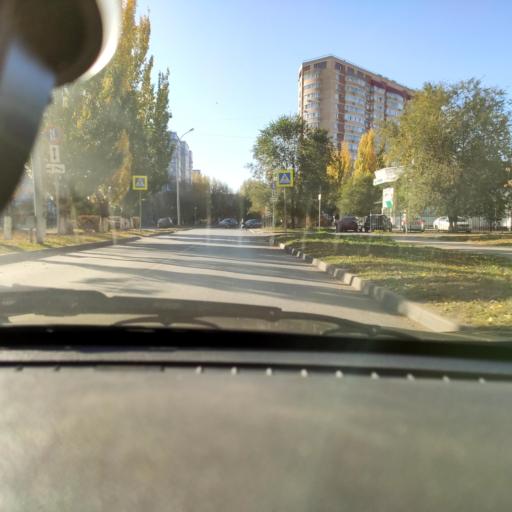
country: RU
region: Samara
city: Tol'yatti
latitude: 53.5419
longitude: 49.3254
